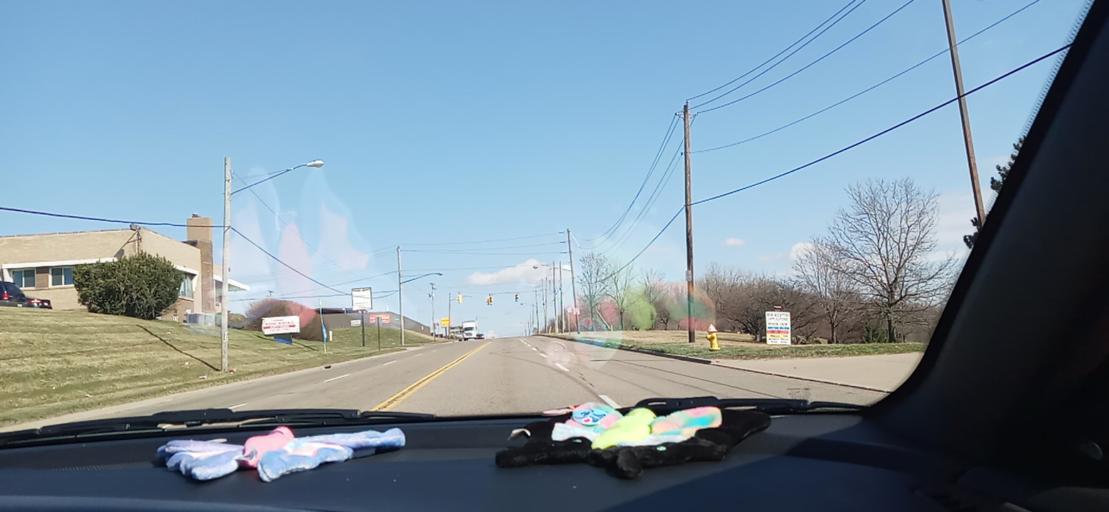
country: US
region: Ohio
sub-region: Summit County
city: Sawyerwood
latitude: 41.0345
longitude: -81.4819
